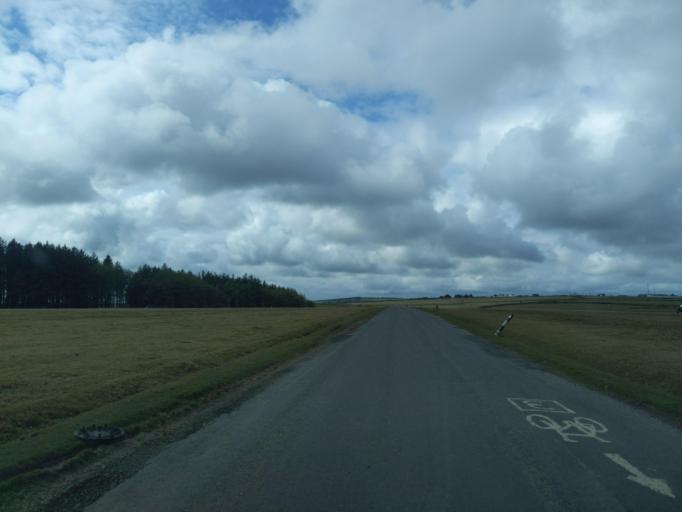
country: GB
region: England
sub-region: Cornwall
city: Camelford
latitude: 50.6389
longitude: -4.6260
